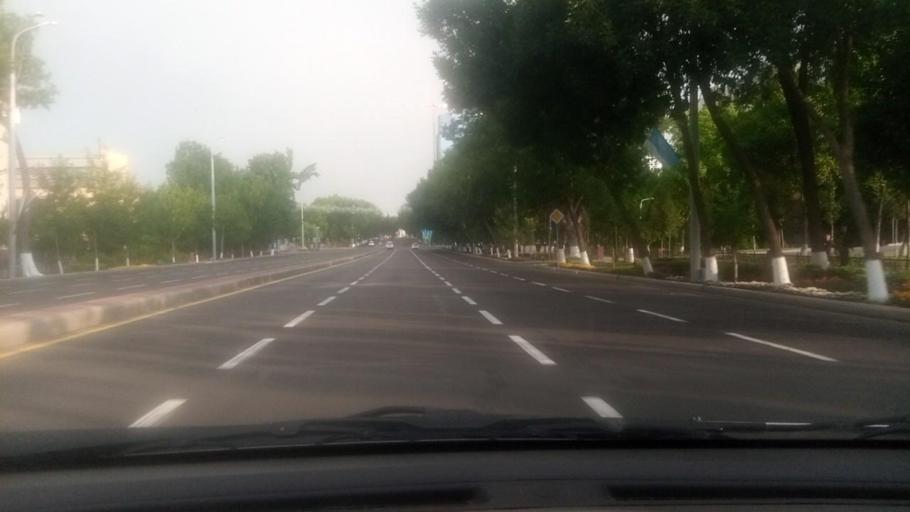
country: UZ
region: Toshkent
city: Salor
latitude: 41.3372
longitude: 69.3413
